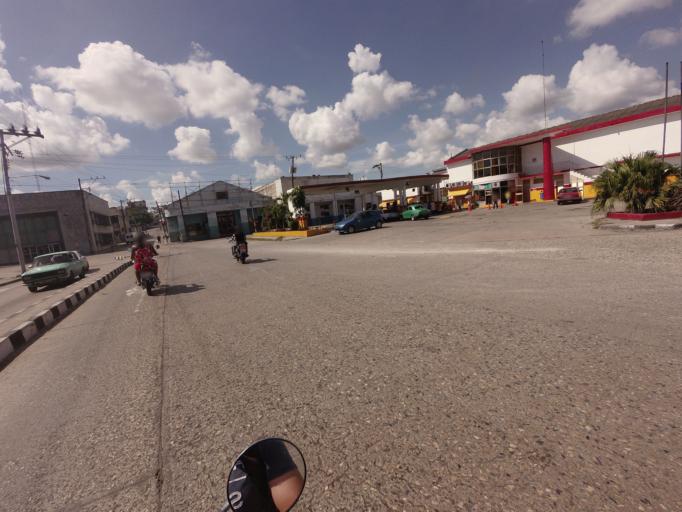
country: CU
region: La Habana
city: La Habana Vieja
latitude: 23.1137
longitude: -82.3593
